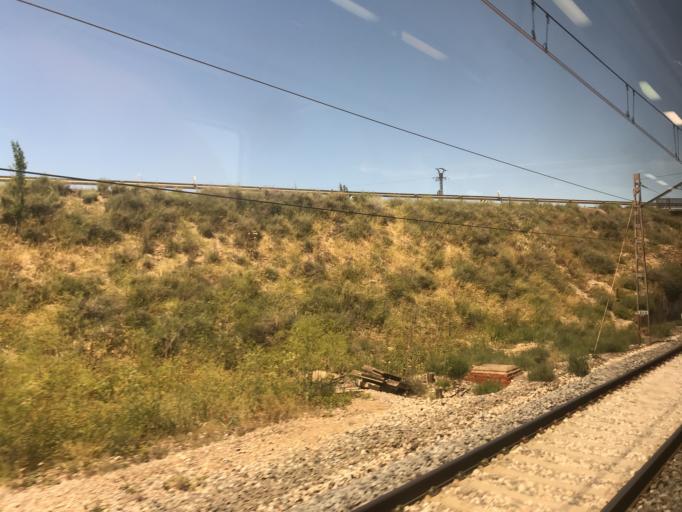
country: ES
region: Madrid
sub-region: Provincia de Madrid
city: Ciempozuelos
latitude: 40.1153
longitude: -3.6211
